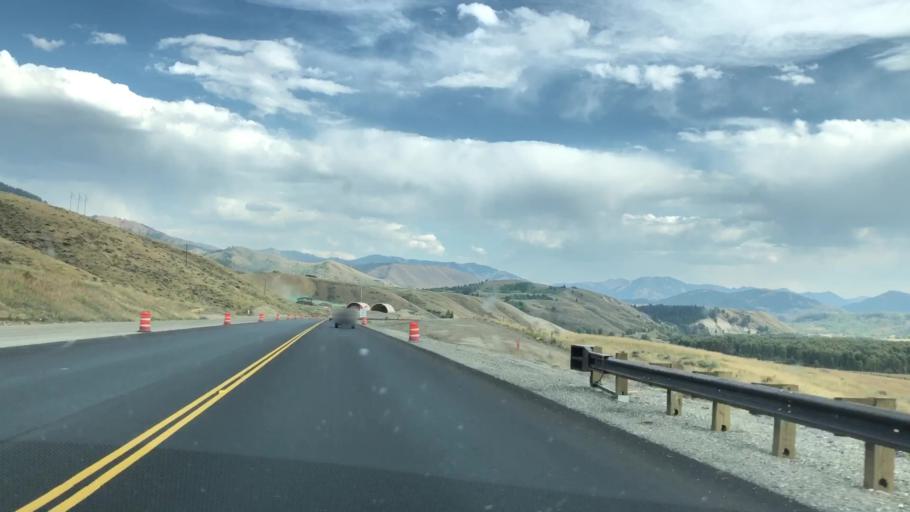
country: US
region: Wyoming
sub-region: Teton County
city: South Park
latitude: 43.4069
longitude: -110.7631
